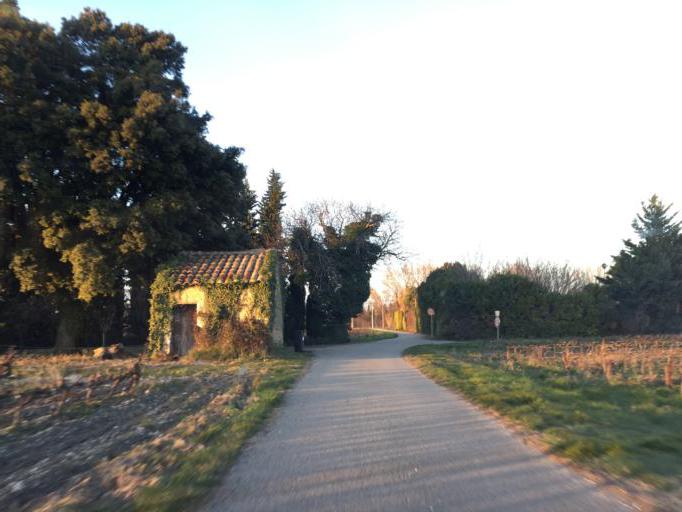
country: FR
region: Provence-Alpes-Cote d'Azur
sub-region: Departement du Vaucluse
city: Camaret-sur-Aigues
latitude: 44.1564
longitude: 4.8961
